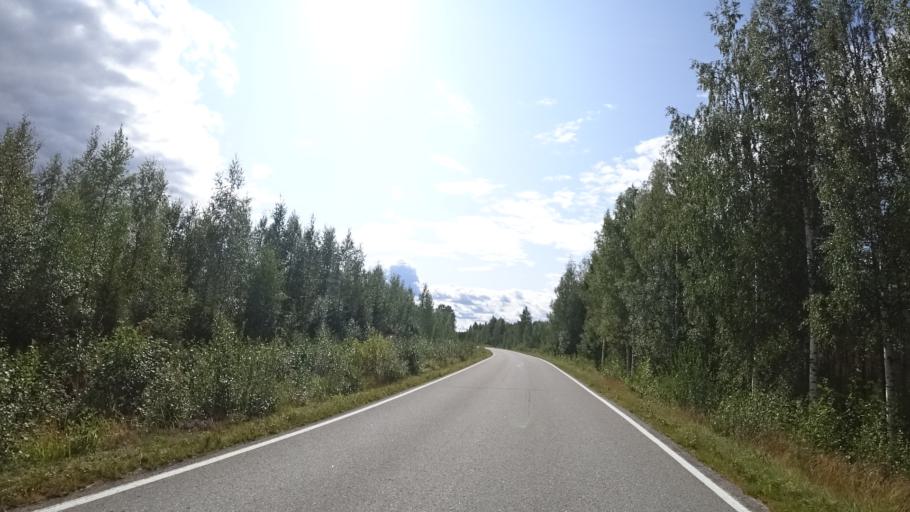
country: FI
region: North Karelia
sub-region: Joensuu
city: Ilomantsi
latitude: 62.4118
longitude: 30.9764
